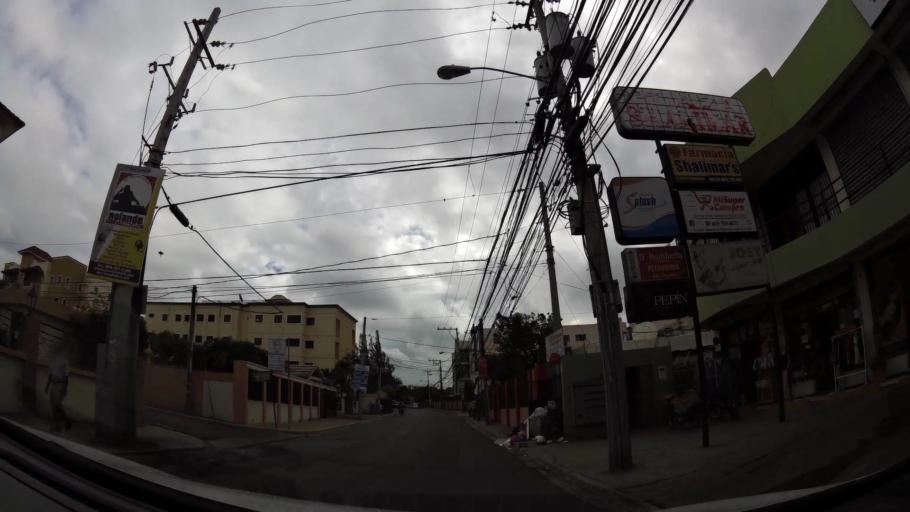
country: DO
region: Santiago
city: Santiago de los Caballeros
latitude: 19.4599
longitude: -70.6613
